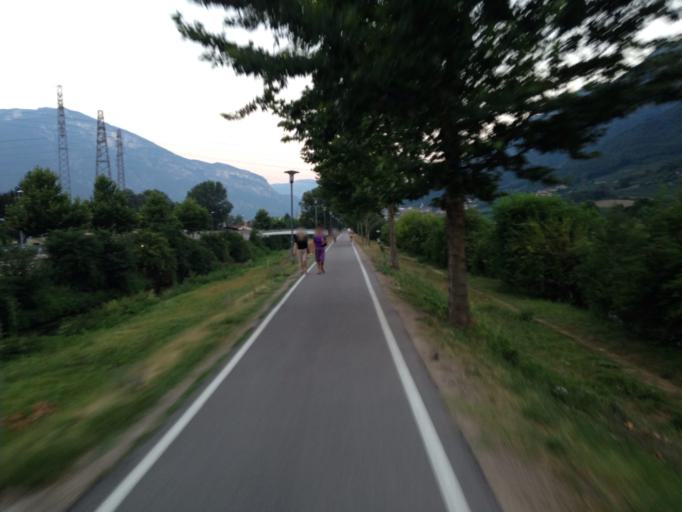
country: IT
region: Trentino-Alto Adige
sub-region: Provincia di Trento
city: Trento
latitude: 46.0583
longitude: 11.1121
